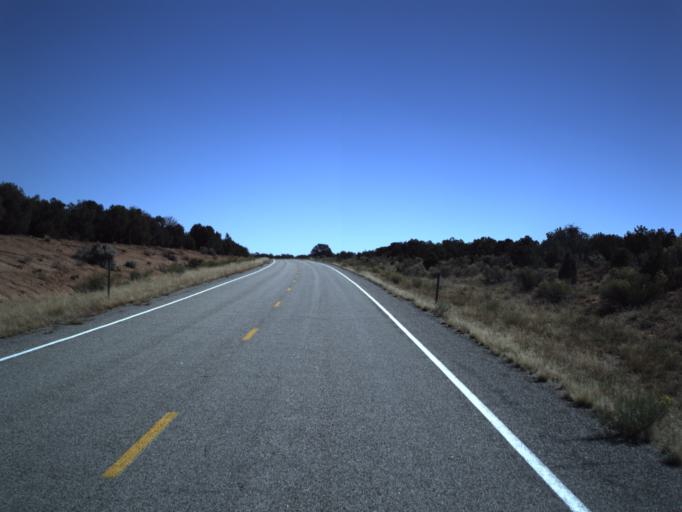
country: US
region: Utah
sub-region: San Juan County
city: Blanding
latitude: 37.5415
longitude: -109.9735
